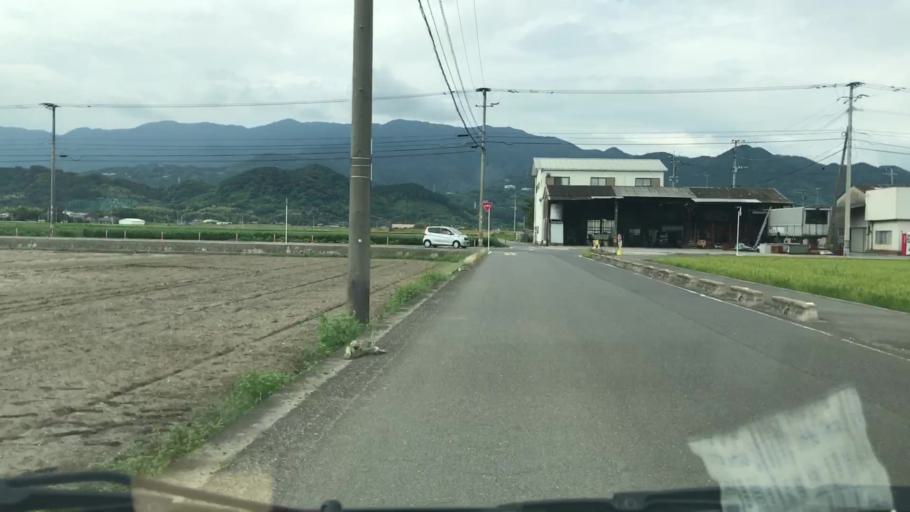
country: JP
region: Saga Prefecture
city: Saga-shi
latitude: 33.2886
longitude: 130.2247
